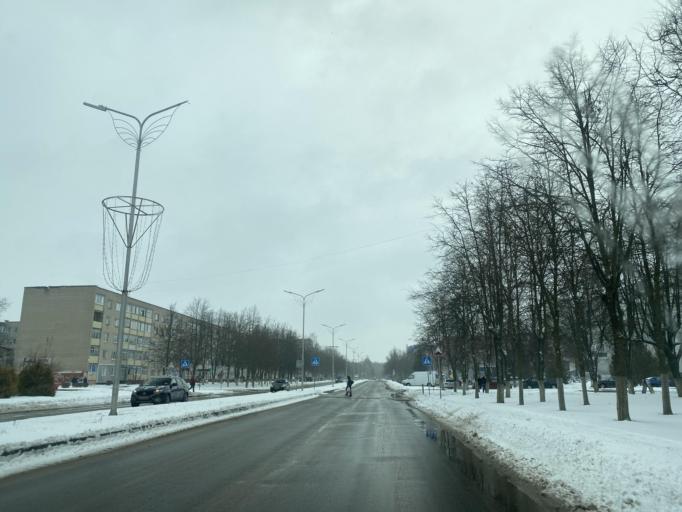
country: BY
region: Minsk
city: Horad Zhodzina
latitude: 54.0945
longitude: 28.3062
